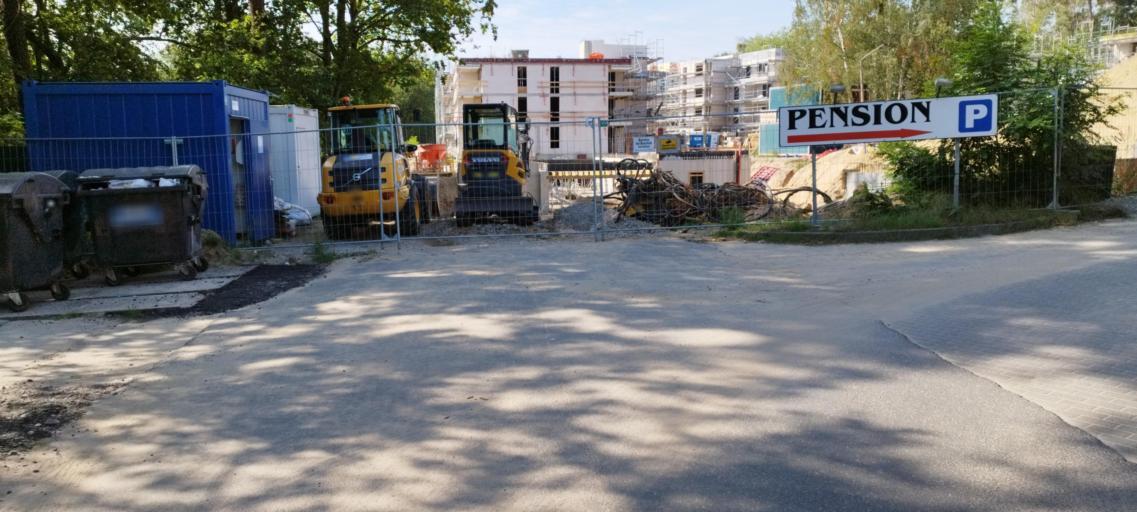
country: DE
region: Brandenburg
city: Dallgow-Doeberitz
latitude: 52.5323
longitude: 13.0547
